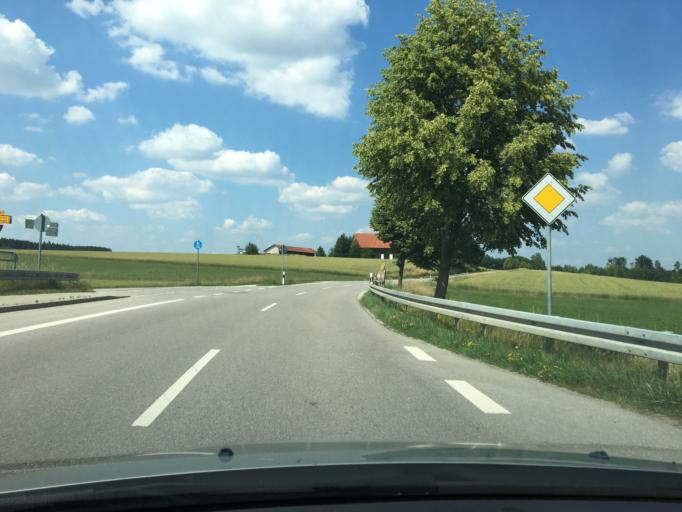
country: DE
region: Bavaria
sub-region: Lower Bavaria
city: Vilsbiburg
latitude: 48.4364
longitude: 12.3437
